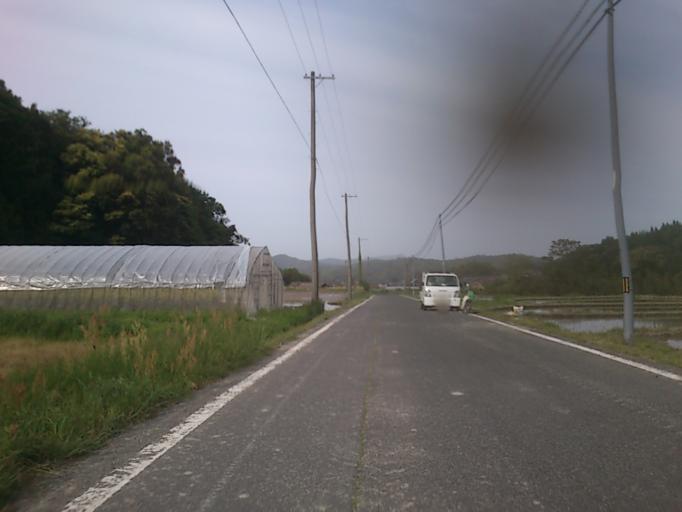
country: JP
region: Kyoto
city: Miyazu
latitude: 35.6420
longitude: 135.0215
